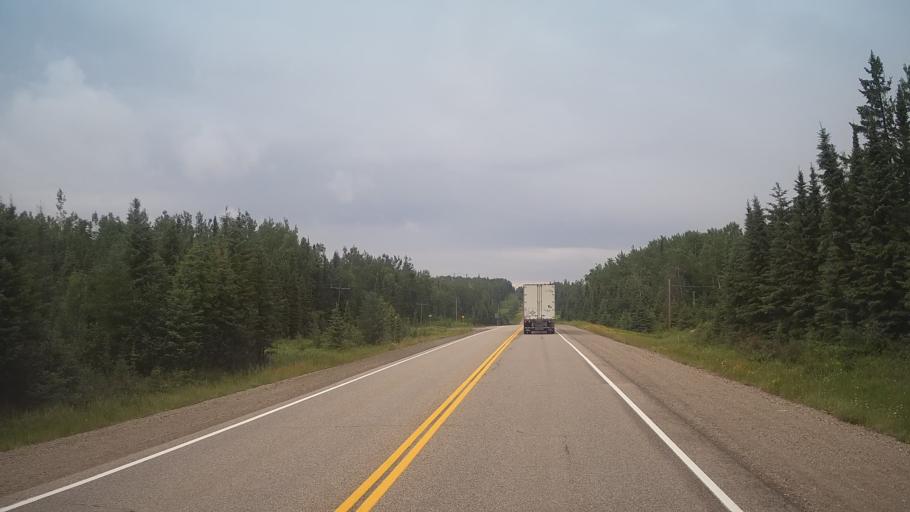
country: CA
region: Ontario
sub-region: Thunder Bay District
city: Thunder Bay
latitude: 48.7547
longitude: -89.8794
